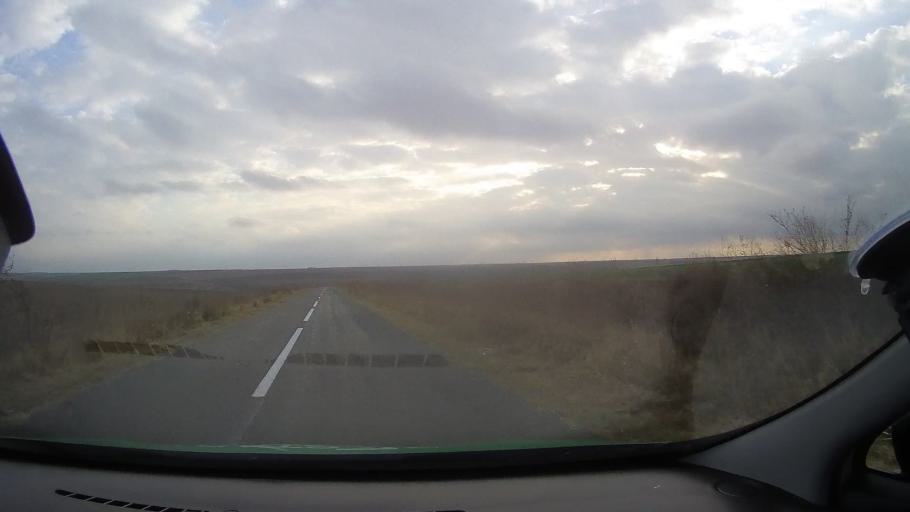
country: RO
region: Constanta
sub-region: Comuna Deleni
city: Pietreni
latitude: 44.1229
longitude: 28.1050
